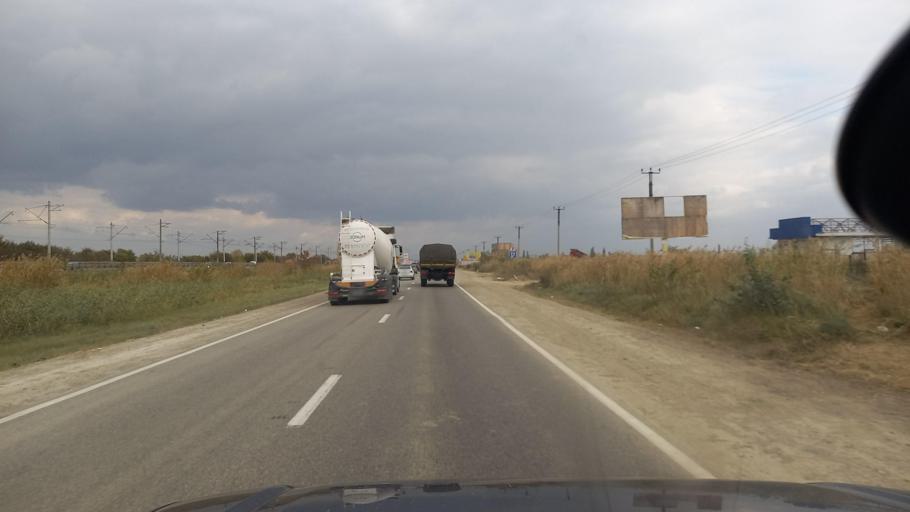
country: RU
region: Adygeya
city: Enem
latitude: 44.9418
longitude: 38.9184
